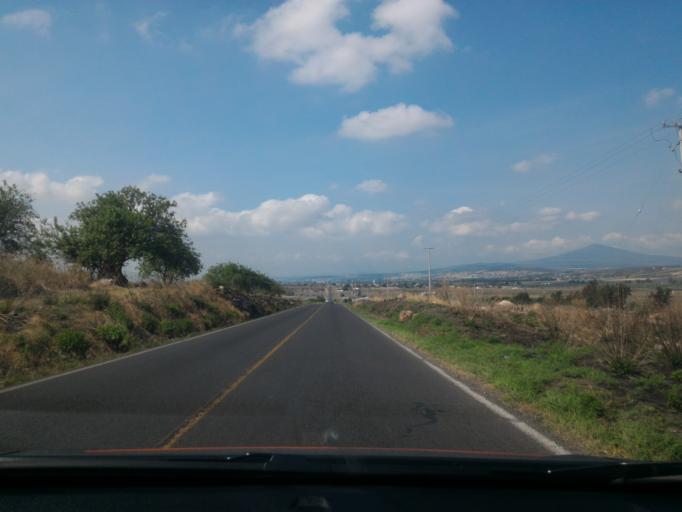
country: MX
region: Guanajuato
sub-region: Penjamo
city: Estacion la Piedad
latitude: 20.4274
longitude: -101.9915
